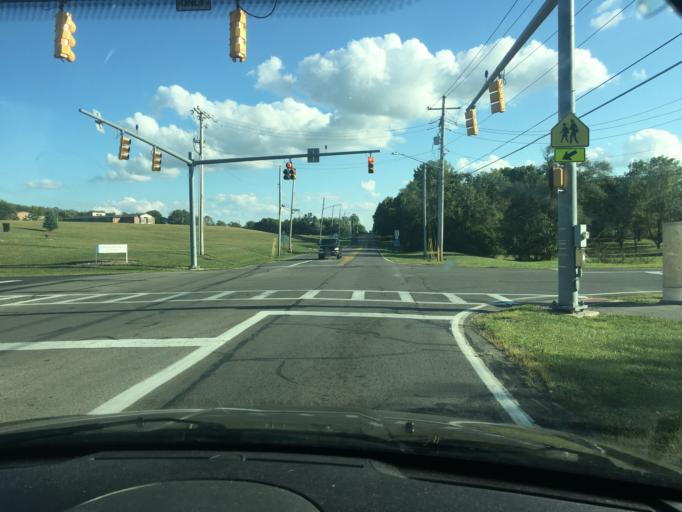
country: US
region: Ohio
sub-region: Logan County
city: Bellefontaine
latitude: 40.3464
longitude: -83.7488
